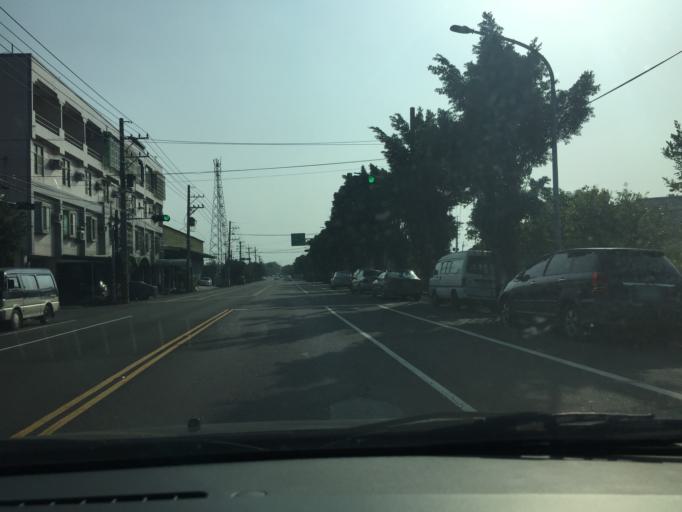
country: TW
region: Taiwan
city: Xinying
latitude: 23.1953
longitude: 120.2842
